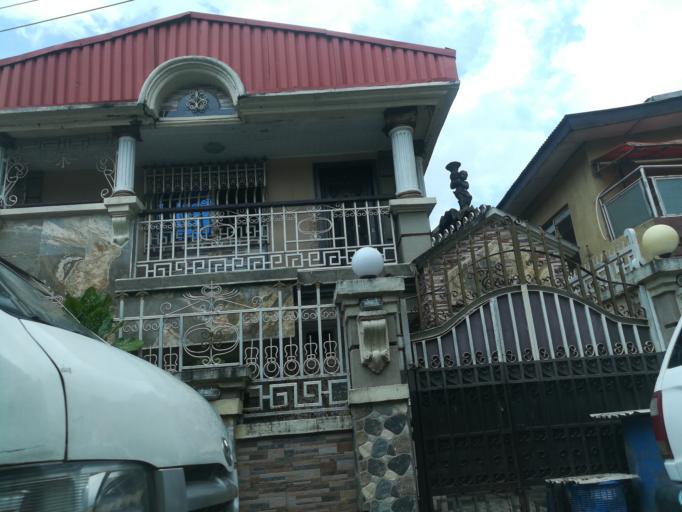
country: NG
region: Lagos
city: Mushin
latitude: 6.5214
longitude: 3.3668
